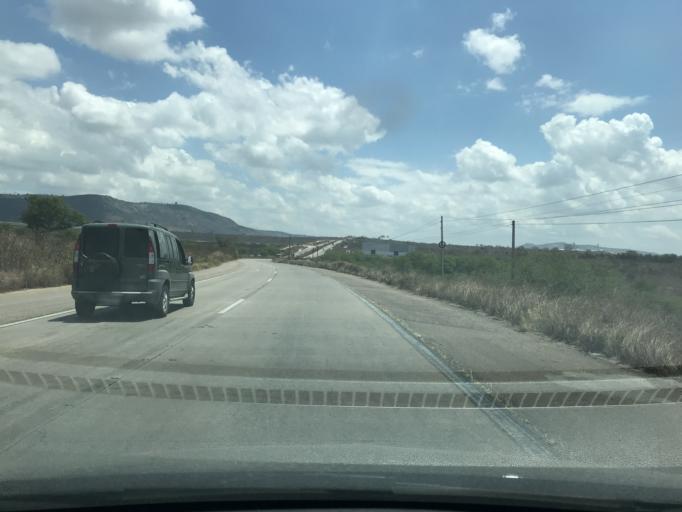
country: BR
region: Pernambuco
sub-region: Bezerros
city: Bezerros
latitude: -8.2880
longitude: -35.8202
